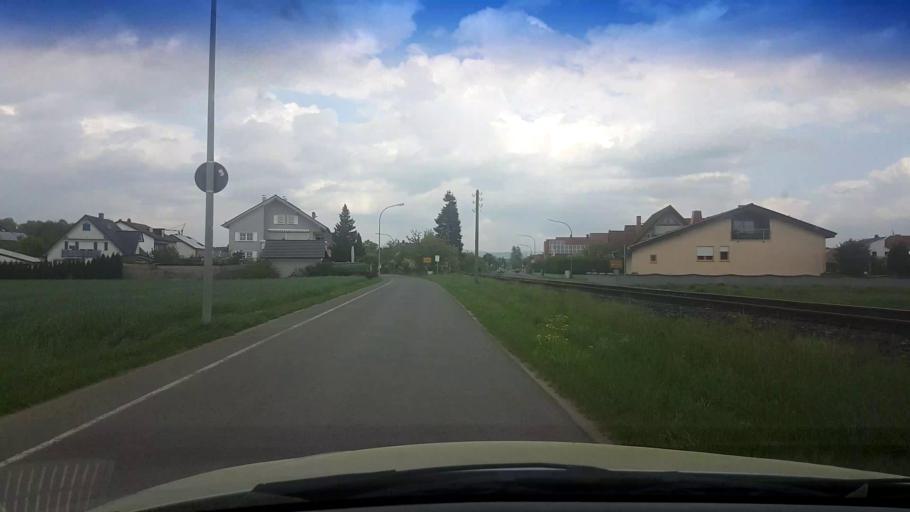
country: DE
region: Bavaria
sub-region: Upper Franconia
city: Pettstadt
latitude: 49.8267
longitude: 10.9210
